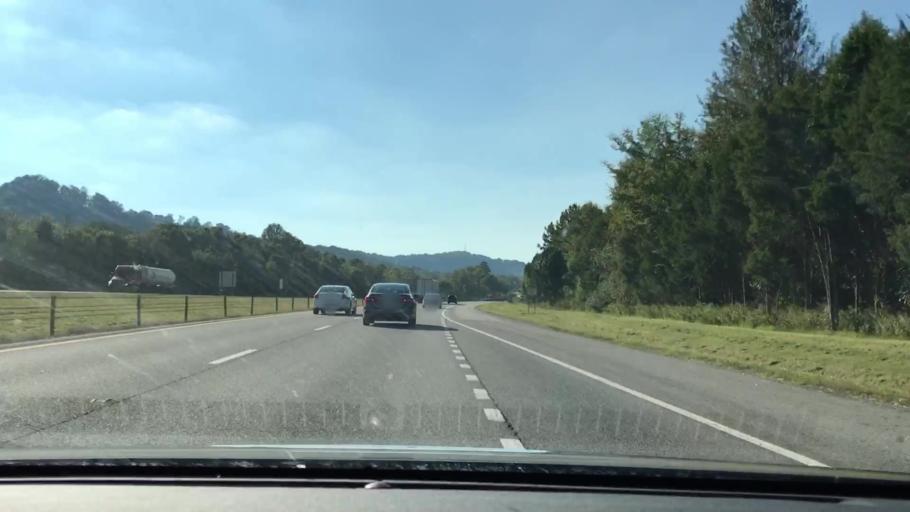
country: US
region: Tennessee
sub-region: Putnam County
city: Lafayette
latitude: 36.1387
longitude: -85.8121
